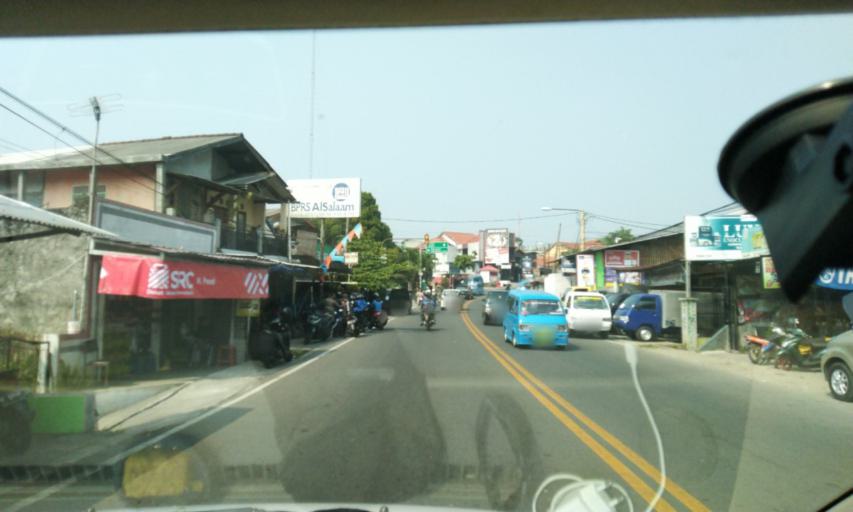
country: ID
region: West Java
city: Caringin
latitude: -6.6617
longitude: 106.8569
